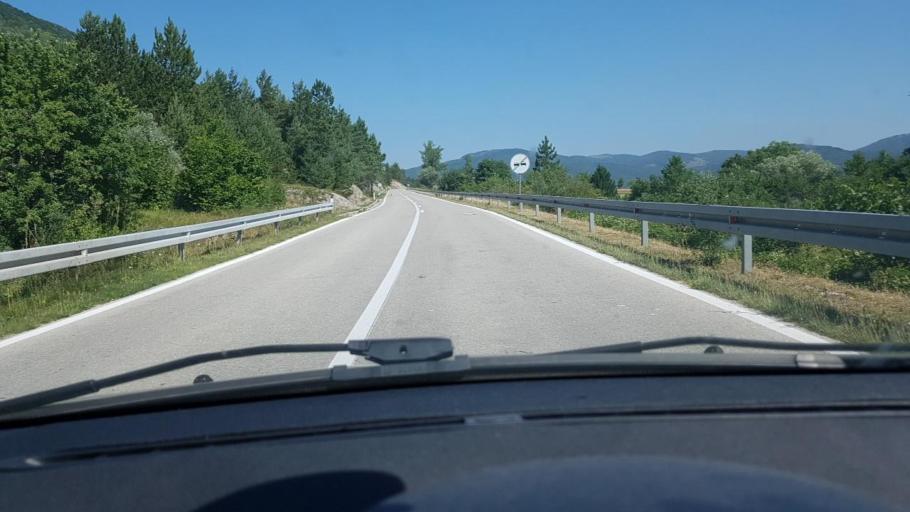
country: BA
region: Federation of Bosnia and Herzegovina
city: Bosansko Grahovo
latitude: 44.2500
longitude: 16.3083
